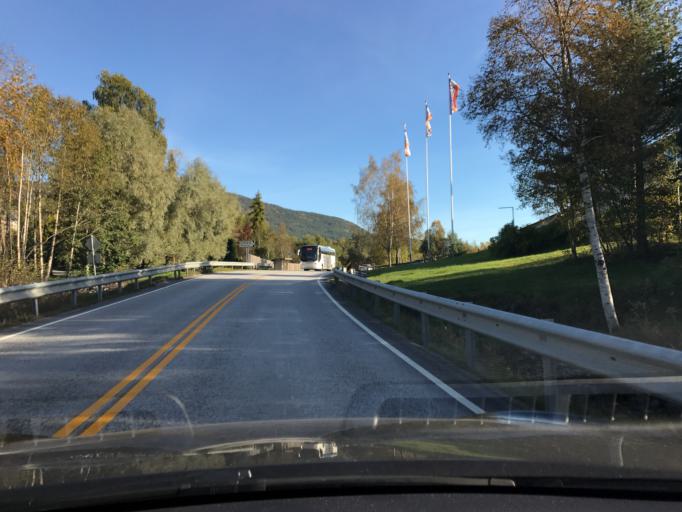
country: NO
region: Sogn og Fjordane
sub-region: Sogndal
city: Sogndalsfjora
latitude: 61.2058
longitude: 7.1989
